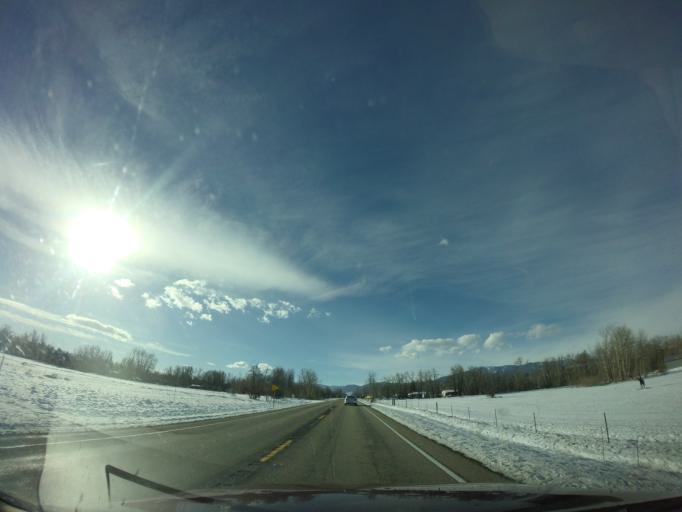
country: US
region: Montana
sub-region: Carbon County
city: Red Lodge
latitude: 45.2641
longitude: -109.2252
